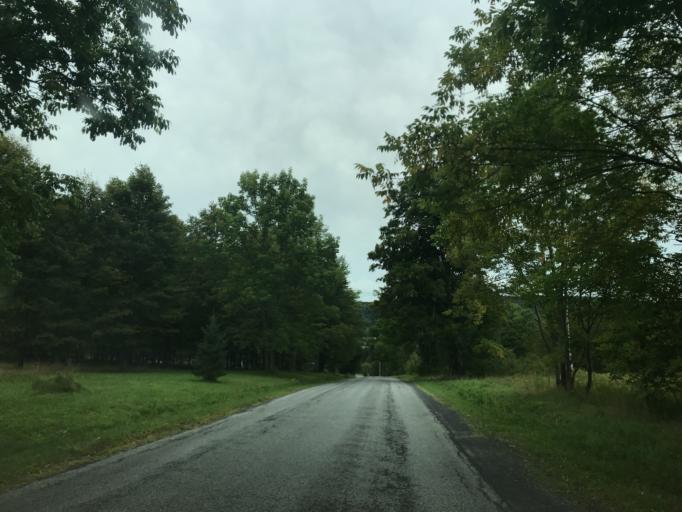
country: US
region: New York
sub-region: Otsego County
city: Worcester
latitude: 42.5501
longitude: -74.6652
